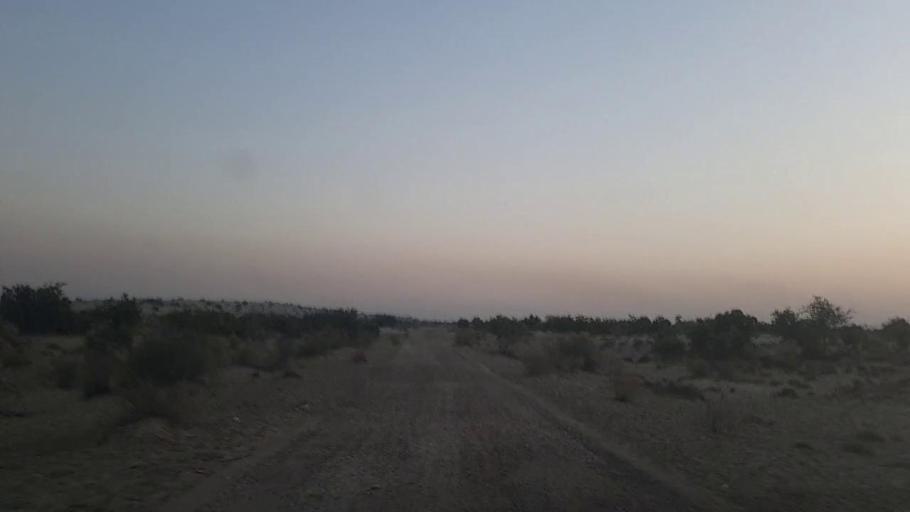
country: PK
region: Sindh
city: Jam Sahib
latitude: 26.4050
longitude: 68.8096
